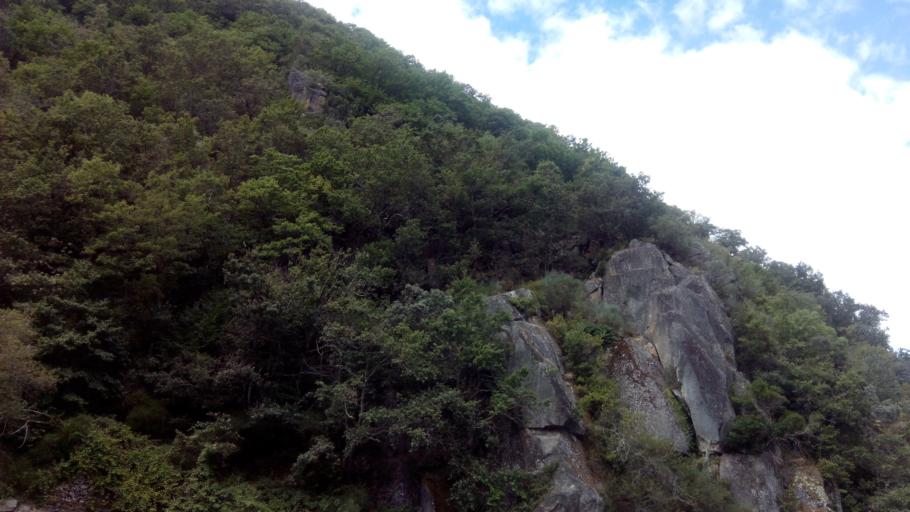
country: ES
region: Galicia
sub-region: Provincia de Lugo
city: Sober
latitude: 42.4016
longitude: -7.6295
